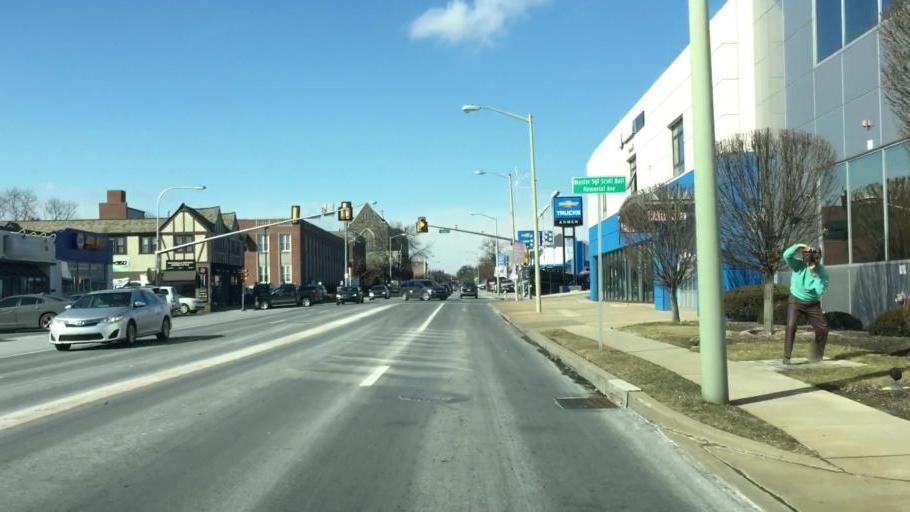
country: US
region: Pennsylvania
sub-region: Montgomery County
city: Ardmore
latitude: 40.0050
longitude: -75.2850
